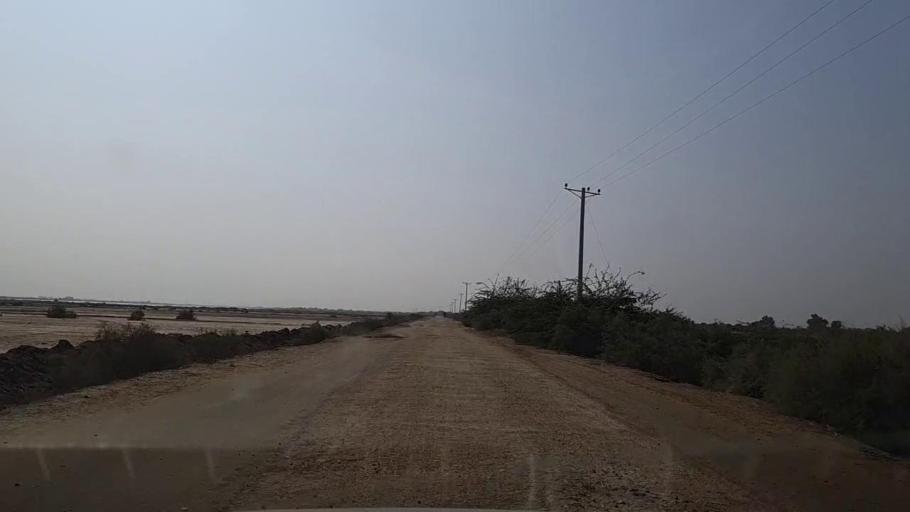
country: PK
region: Sindh
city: Mirpur Sakro
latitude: 24.5413
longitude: 67.6033
